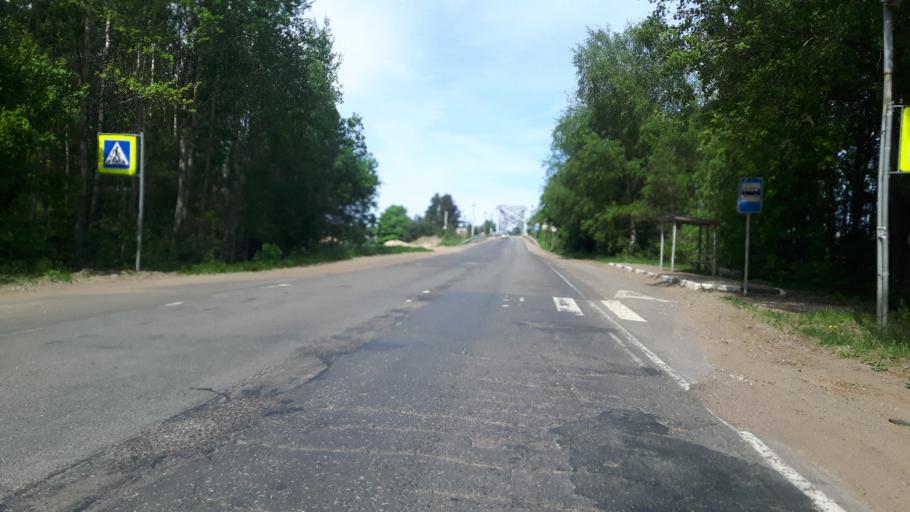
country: RU
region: Leningrad
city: Ust'-Luga
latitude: 59.6505
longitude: 28.2608
